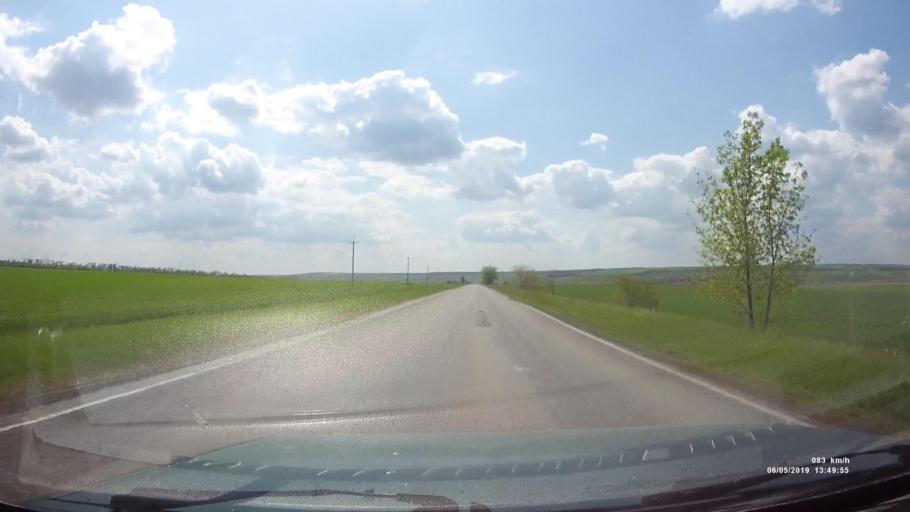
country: RU
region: Rostov
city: Melikhovskaya
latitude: 47.6573
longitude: 40.5157
